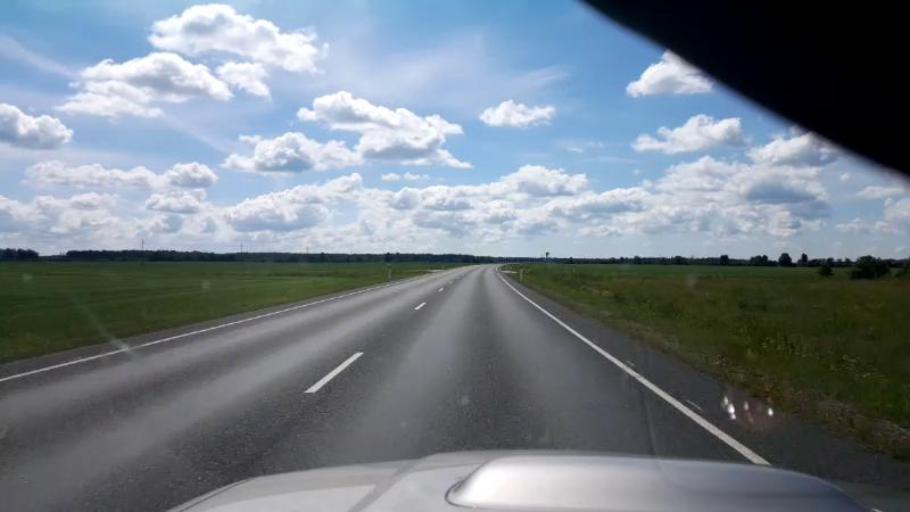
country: EE
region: Jaervamaa
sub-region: Jaerva-Jaani vald
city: Jarva-Jaani
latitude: 59.1502
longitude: 25.7698
